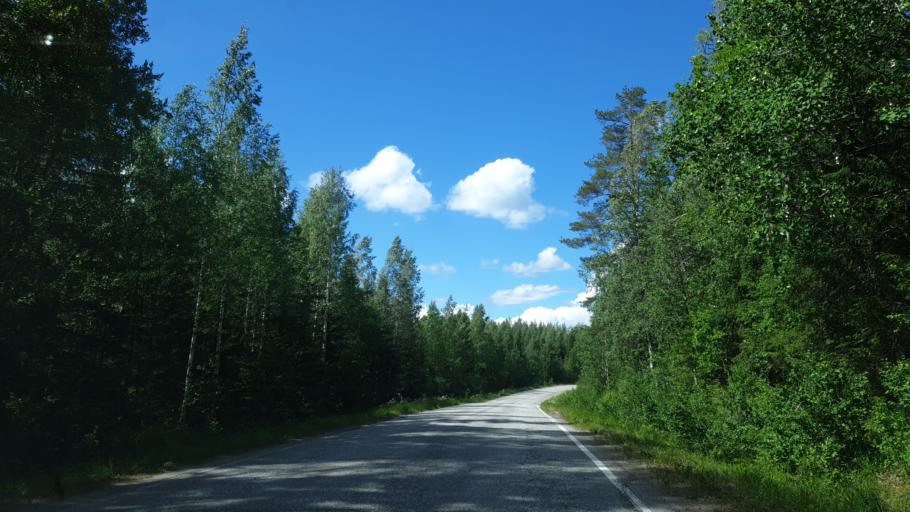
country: FI
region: Northern Savo
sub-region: Koillis-Savo
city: Kaavi
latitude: 63.0370
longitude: 28.6022
